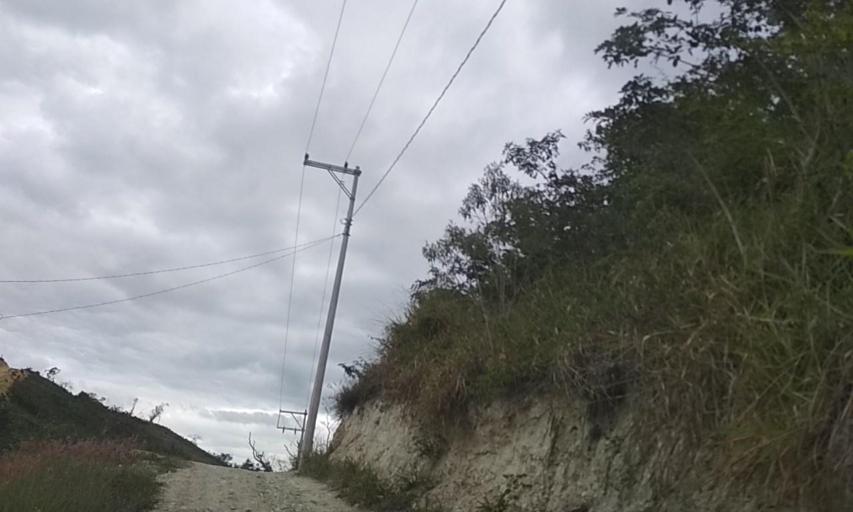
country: MX
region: Veracruz
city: Papantla de Olarte
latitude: 20.4602
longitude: -97.3170
